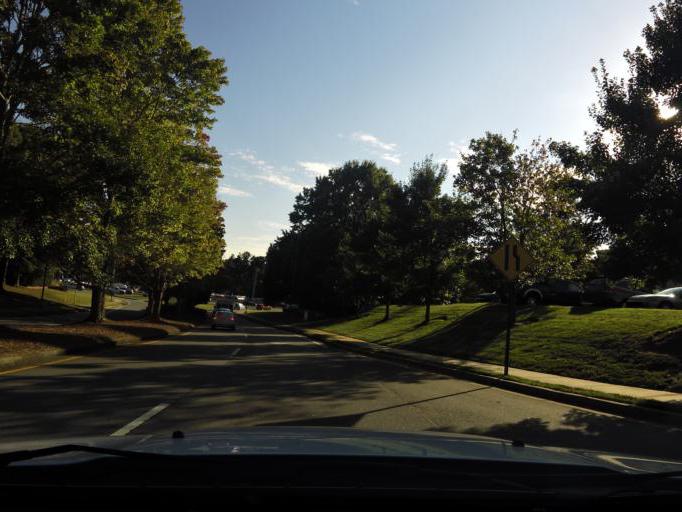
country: US
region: Georgia
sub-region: Cobb County
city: Kennesaw
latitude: 34.0034
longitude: -84.5964
